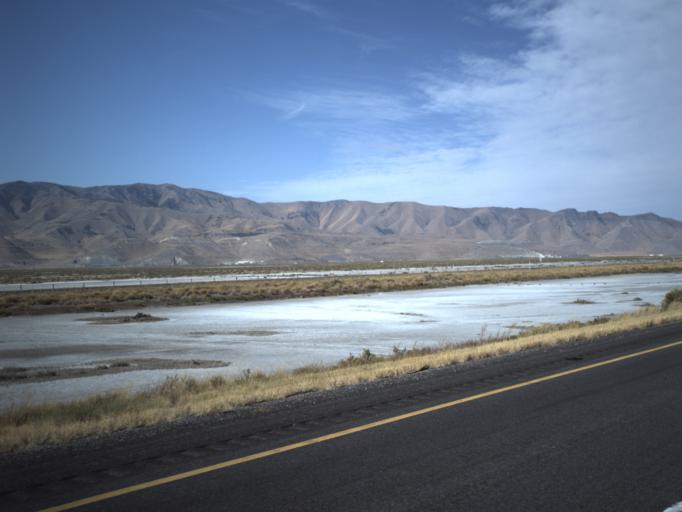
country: US
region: Utah
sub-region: Tooele County
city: Grantsville
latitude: 40.6980
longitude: -112.4799
